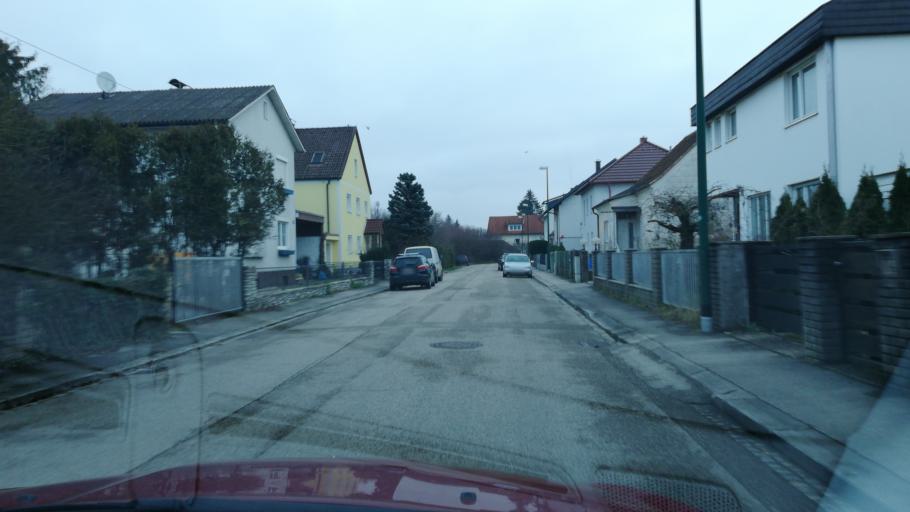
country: AT
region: Upper Austria
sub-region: Wels Stadt
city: Wels
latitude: 48.1760
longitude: 14.0532
